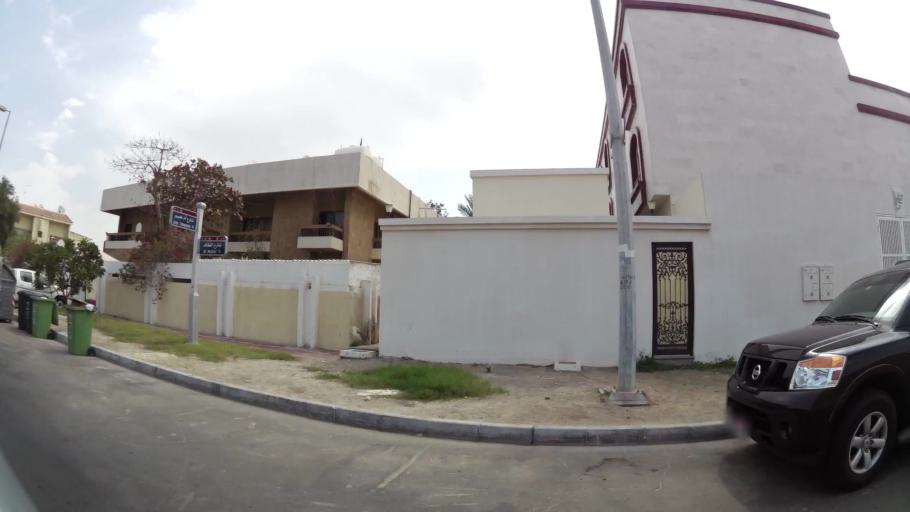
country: AE
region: Abu Dhabi
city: Abu Dhabi
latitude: 24.4597
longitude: 54.3501
